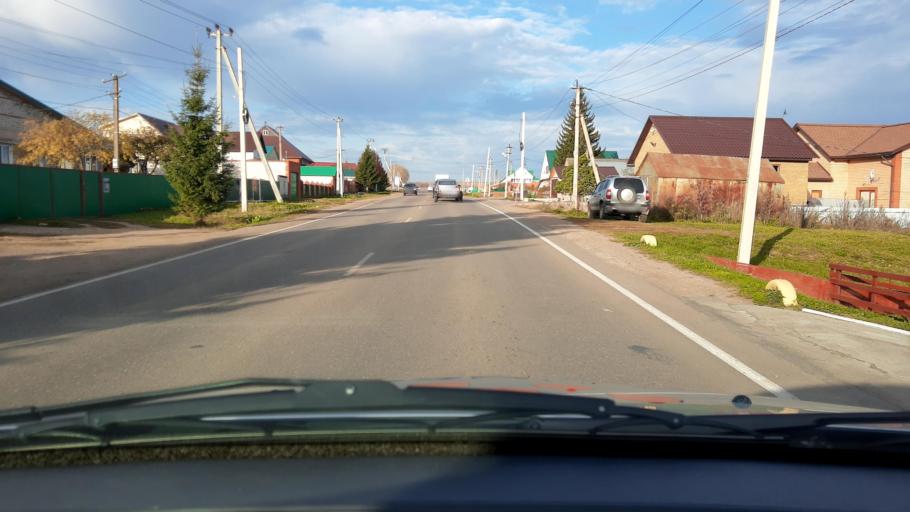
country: RU
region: Bashkortostan
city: Mikhaylovka
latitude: 54.8164
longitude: 55.7927
